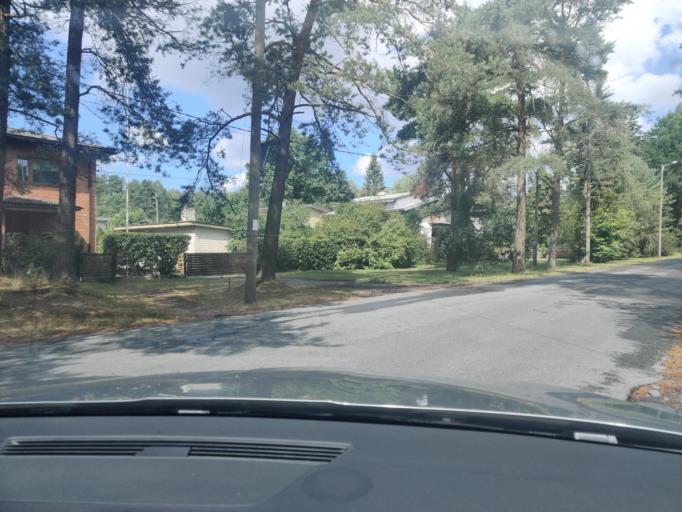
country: EE
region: Harju
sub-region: Saue vald
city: Laagri
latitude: 59.3559
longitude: 24.6201
